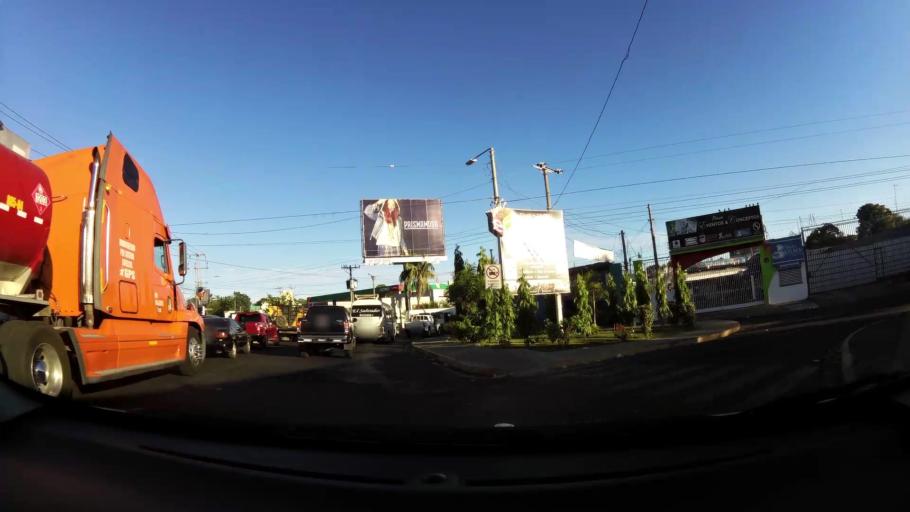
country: SV
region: San Miguel
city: San Miguel
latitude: 13.4867
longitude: -88.1858
